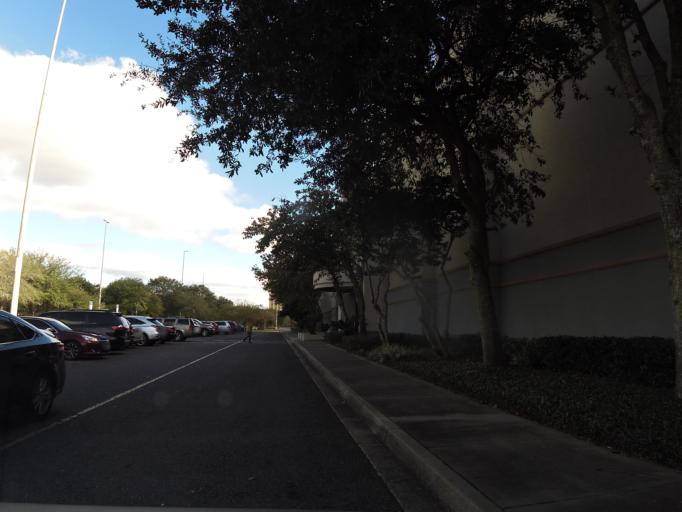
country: US
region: Florida
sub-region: Duval County
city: Jacksonville
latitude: 30.3255
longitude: -81.5553
